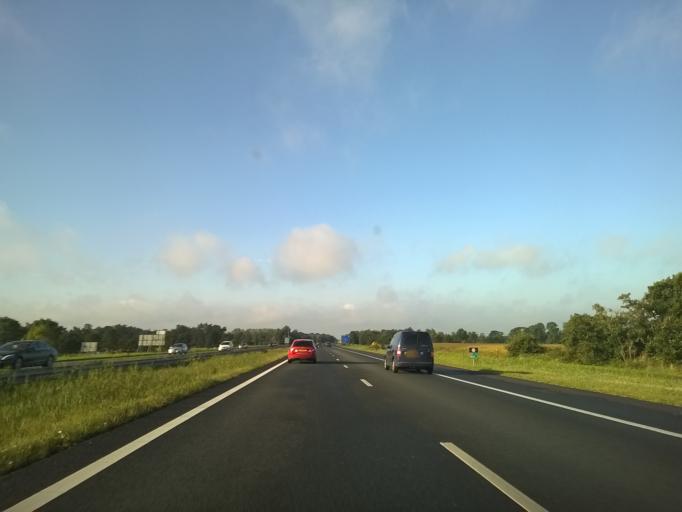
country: NL
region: Groningen
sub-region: Gemeente Leek
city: Leek
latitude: 53.1799
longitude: 6.3655
